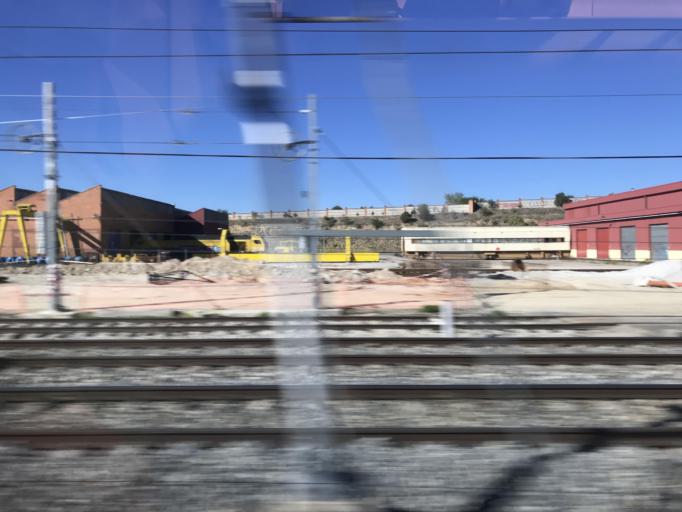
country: ES
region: Madrid
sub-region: Provincia de Madrid
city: Las Tablas
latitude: 40.5089
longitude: -3.6820
